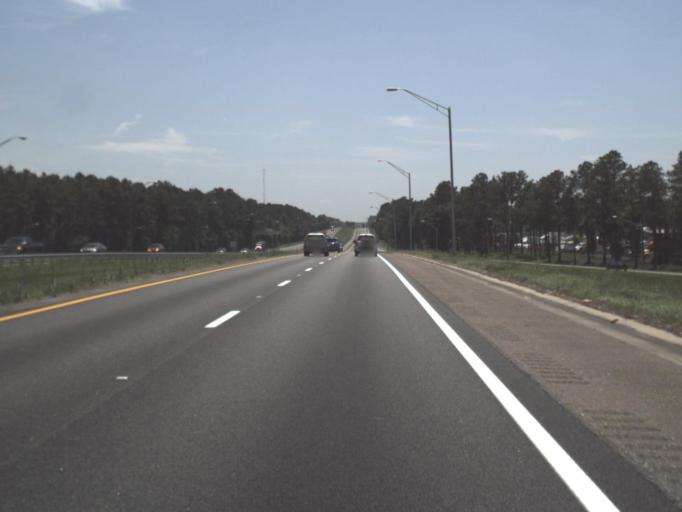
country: US
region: Florida
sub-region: Duval County
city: Jacksonville
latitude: 30.3716
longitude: -81.7612
